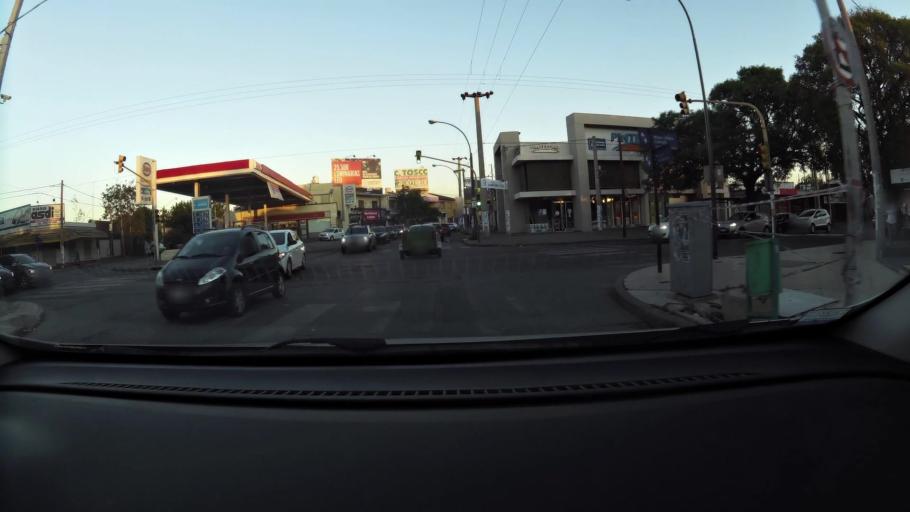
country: AR
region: Cordoba
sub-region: Departamento de Capital
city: Cordoba
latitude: -31.3766
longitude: -64.2069
